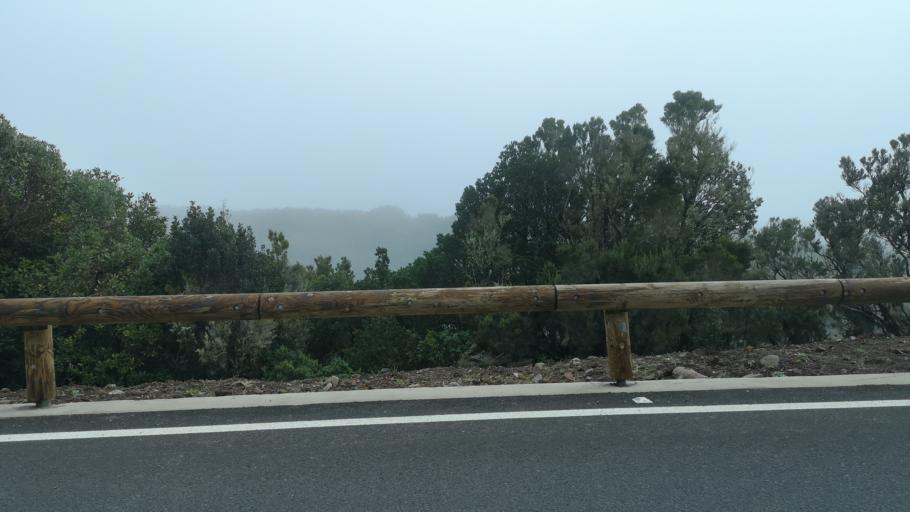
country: ES
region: Canary Islands
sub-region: Provincia de Santa Cruz de Tenerife
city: Vallehermosa
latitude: 28.1492
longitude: -17.3083
